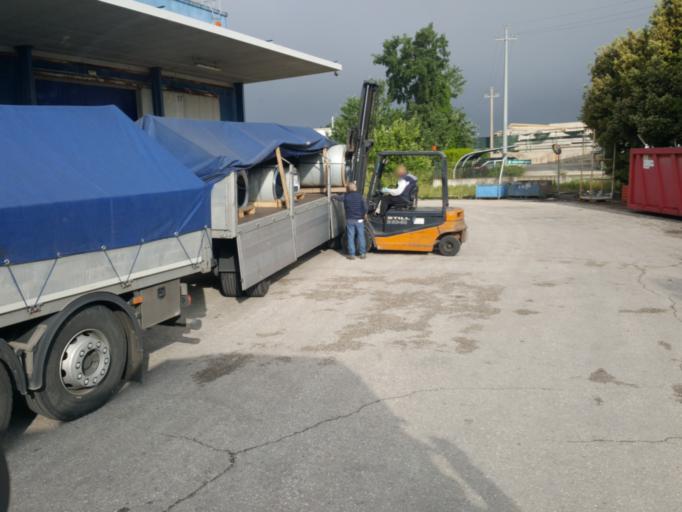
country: IT
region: Umbria
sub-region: Provincia di Perugia
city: Bastia umbra
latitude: 43.0523
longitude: 12.5477
